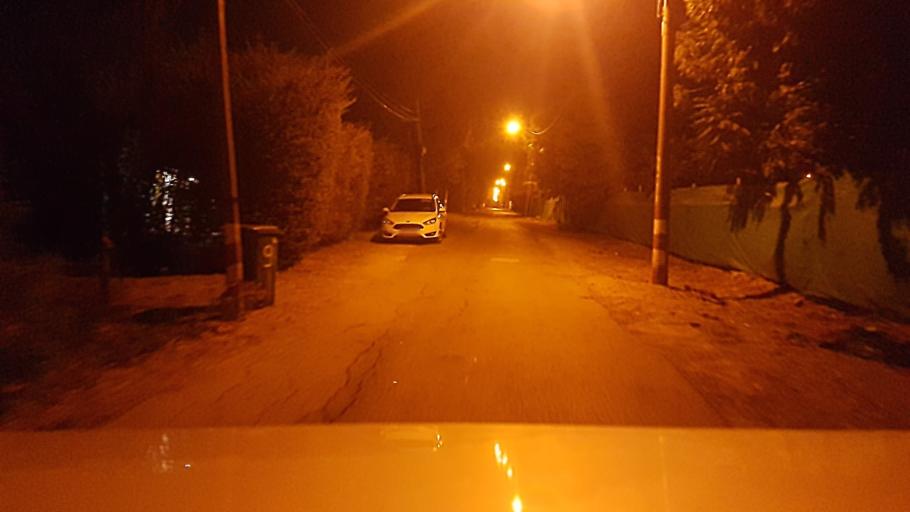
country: IL
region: Central District
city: Nehalim
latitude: 32.0804
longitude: 34.9248
